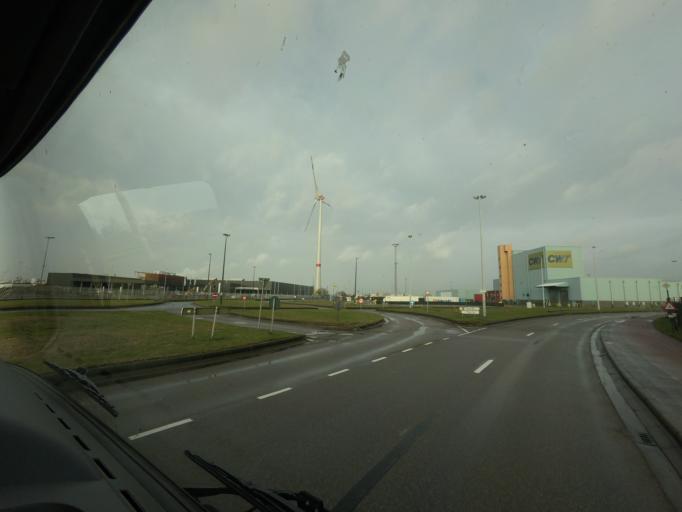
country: BE
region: Flanders
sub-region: Provincie Antwerpen
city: Stabroek
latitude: 51.3124
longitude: 4.3237
